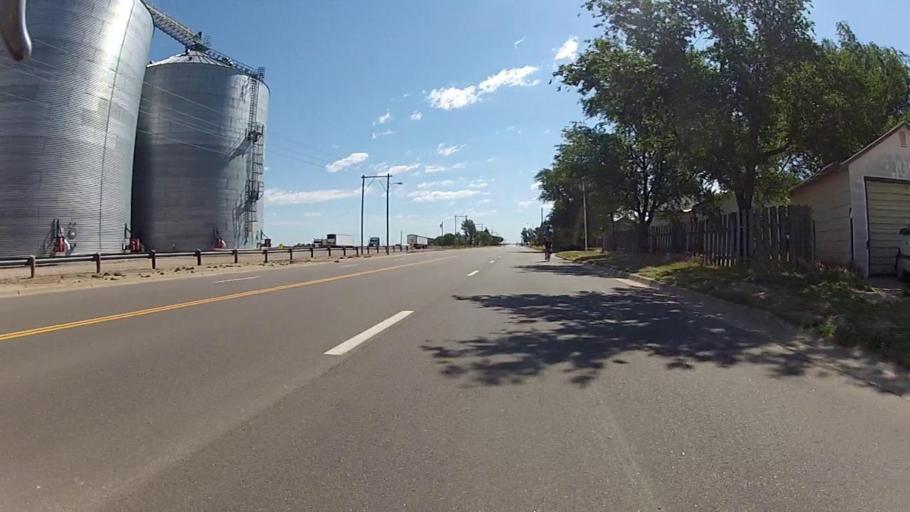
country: US
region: Kansas
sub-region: Gray County
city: Cimarron
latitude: 37.5993
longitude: -100.4420
